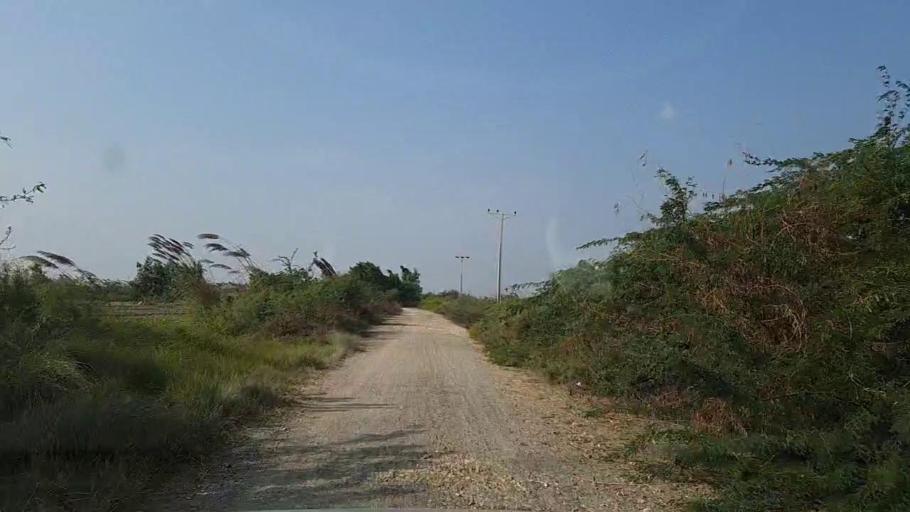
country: PK
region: Sindh
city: Mirpur Sakro
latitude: 24.5787
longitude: 67.5685
